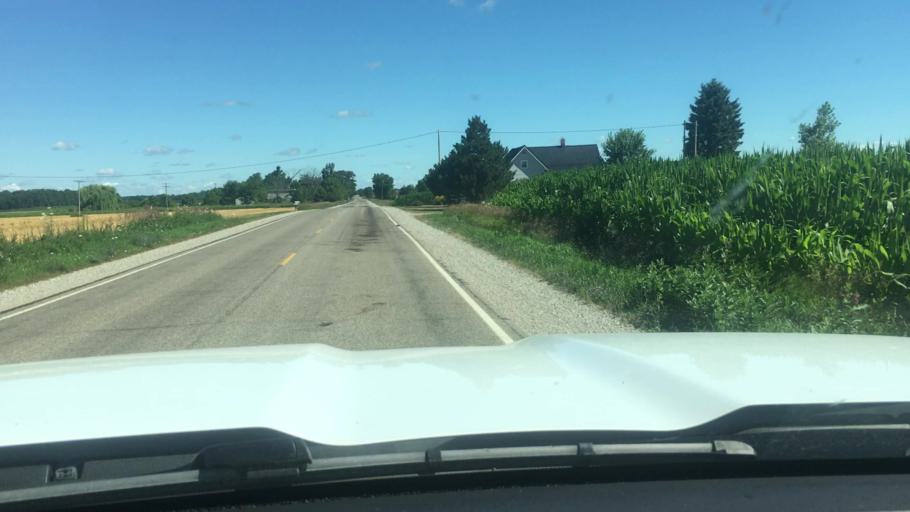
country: US
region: Michigan
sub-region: Montcalm County
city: Carson City
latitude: 43.2143
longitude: -84.7778
